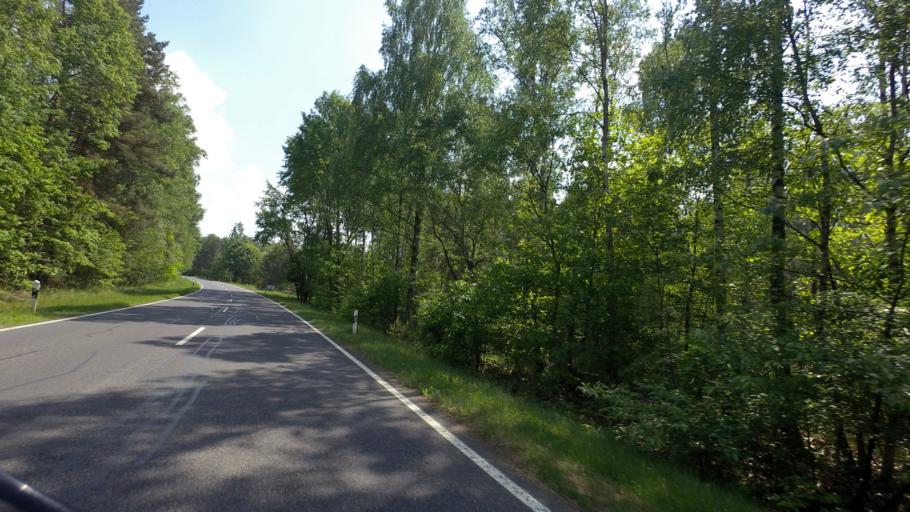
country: DE
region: Saxony
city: Schleife
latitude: 51.5527
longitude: 14.5052
